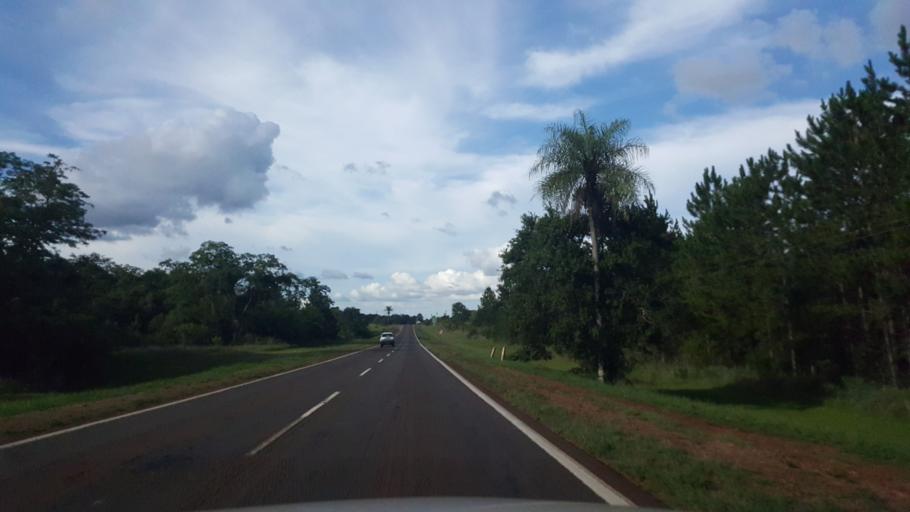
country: AR
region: Misiones
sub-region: Departamento de Candelaria
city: Loreto
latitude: -27.3429
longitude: -55.5460
